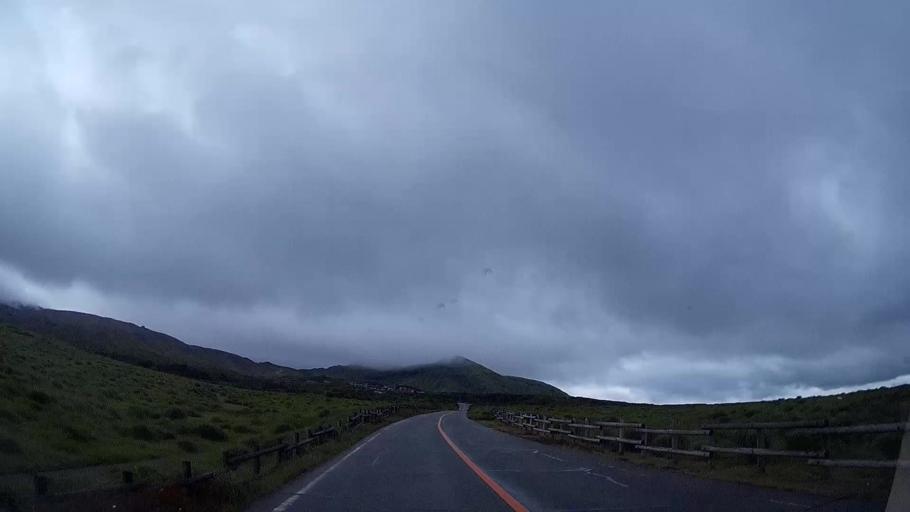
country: JP
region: Kumamoto
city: Aso
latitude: 32.8830
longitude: 131.0668
